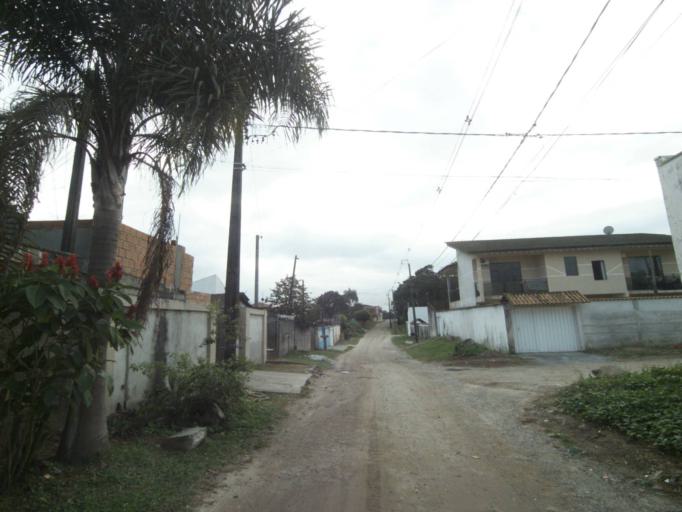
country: BR
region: Parana
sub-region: Paranagua
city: Paranagua
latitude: -25.5343
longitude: -48.5496
